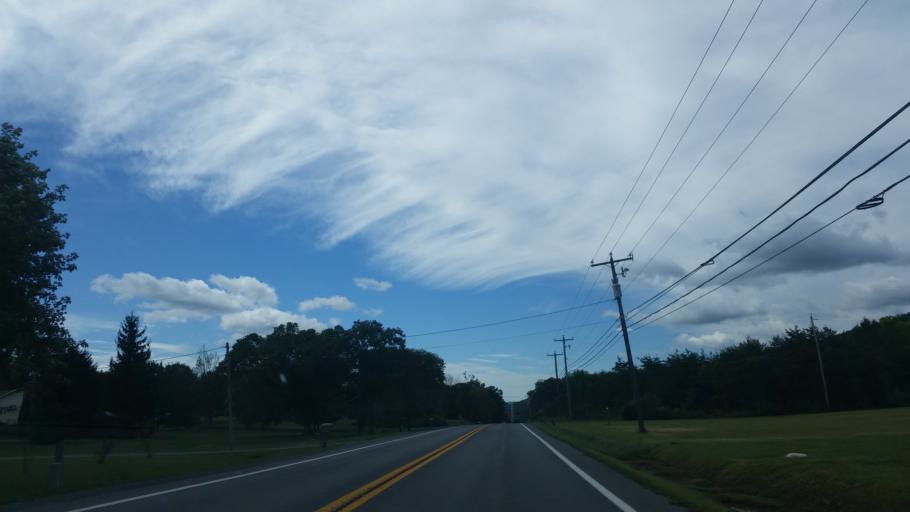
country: US
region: West Virginia
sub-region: Morgan County
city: Berkeley Springs
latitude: 39.5458
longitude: -78.2707
